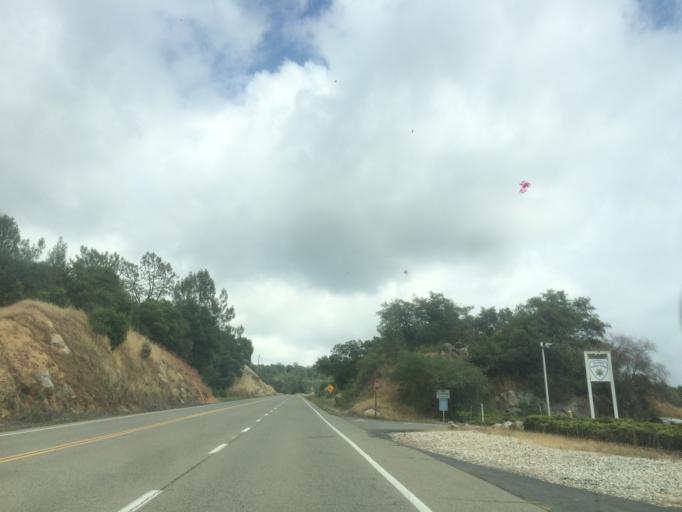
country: US
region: California
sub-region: Placer County
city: Newcastle
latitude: 38.8724
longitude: -121.1283
